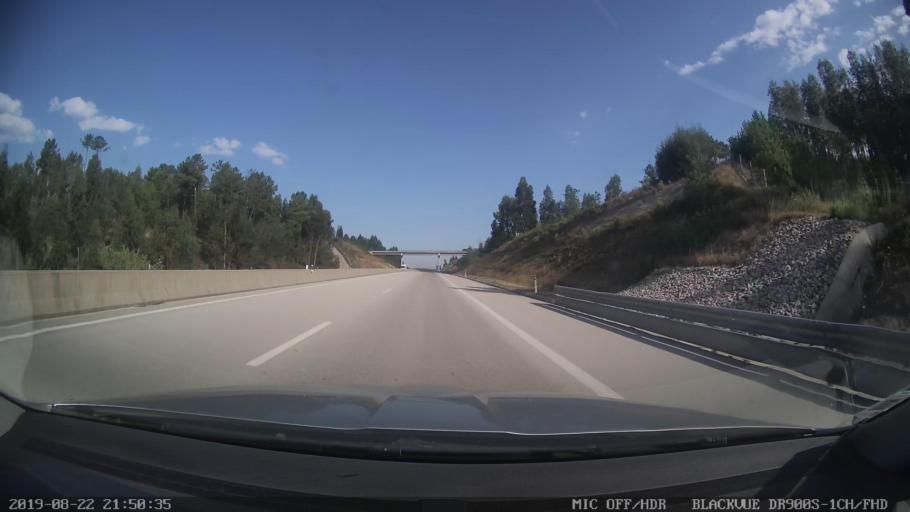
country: PT
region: Coimbra
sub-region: Penela
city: Penela
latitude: 40.0653
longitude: -8.3768
